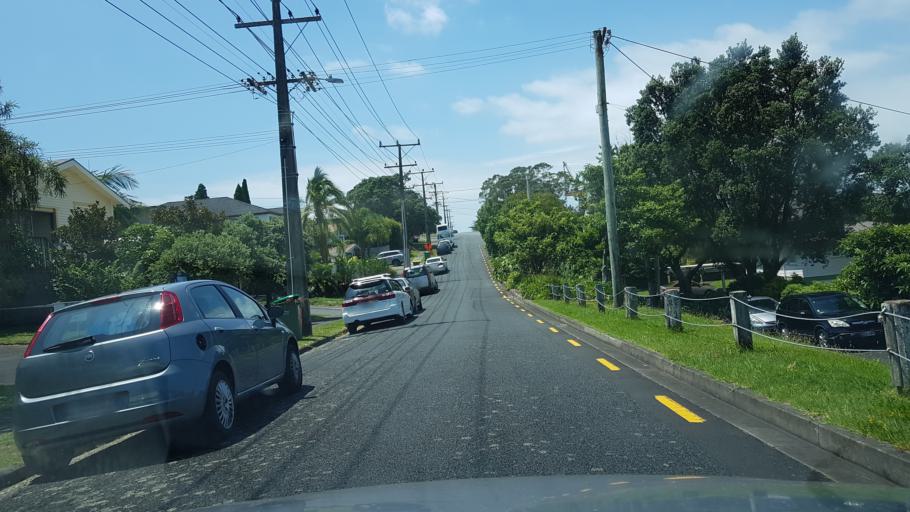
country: NZ
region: Auckland
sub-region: Auckland
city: North Shore
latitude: -36.8178
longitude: 174.7876
